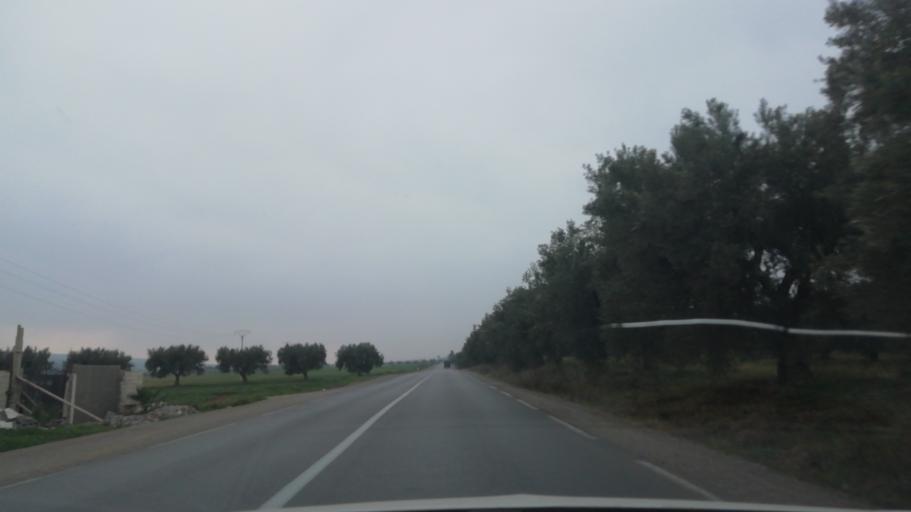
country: DZ
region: Sidi Bel Abbes
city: Sfizef
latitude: 35.2664
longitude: -0.1644
